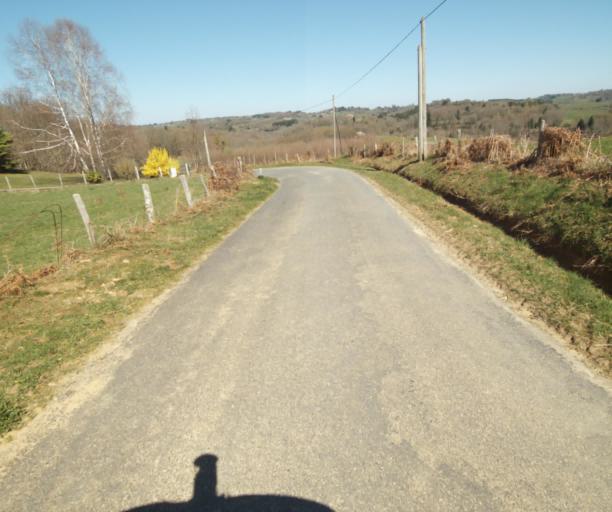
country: FR
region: Limousin
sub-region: Departement de la Correze
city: Saint-Clement
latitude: 45.3121
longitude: 1.6983
